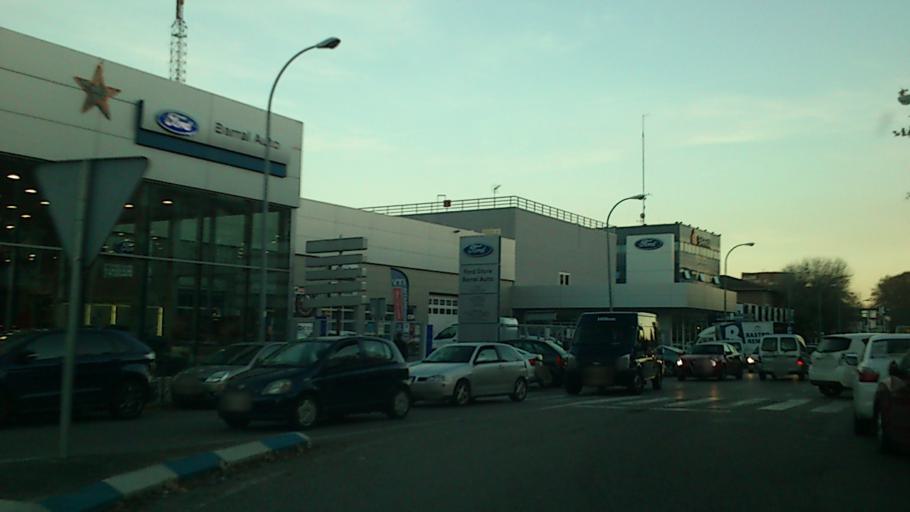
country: ES
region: Madrid
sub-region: Provincia de Madrid
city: San Fernando de Henares
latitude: 40.4324
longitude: -3.5393
